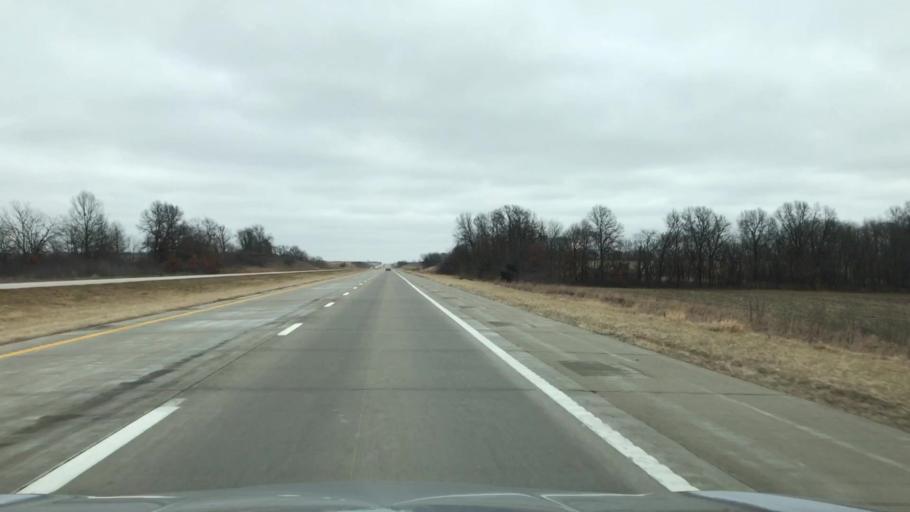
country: US
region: Missouri
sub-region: Caldwell County
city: Hamilton
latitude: 39.7354
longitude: -93.9195
